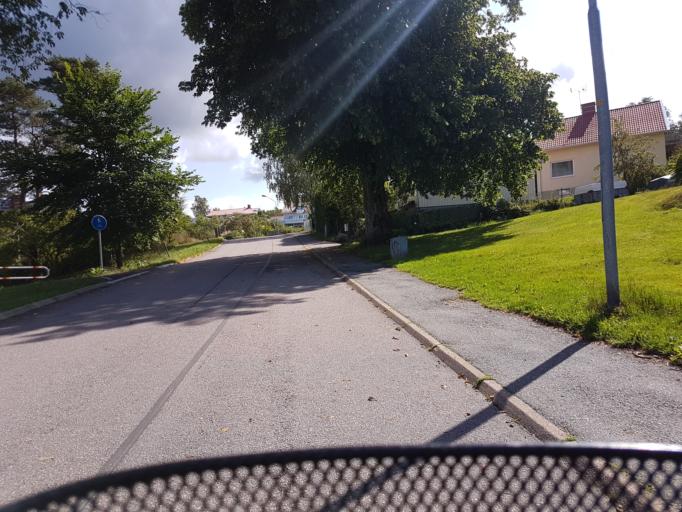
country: SE
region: Vaestra Goetaland
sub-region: Ale Kommun
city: Alvangen
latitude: 57.9593
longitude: 12.1291
